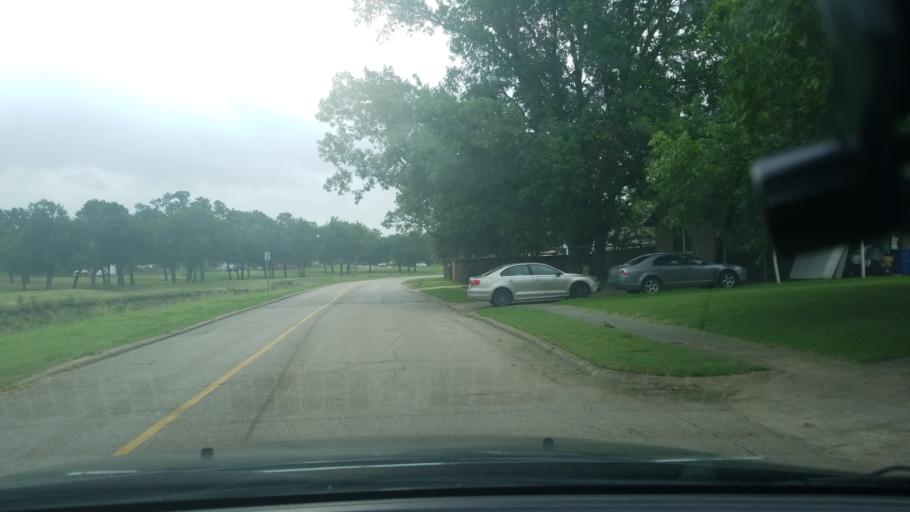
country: US
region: Texas
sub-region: Dallas County
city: Mesquite
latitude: 32.7874
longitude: -96.6383
